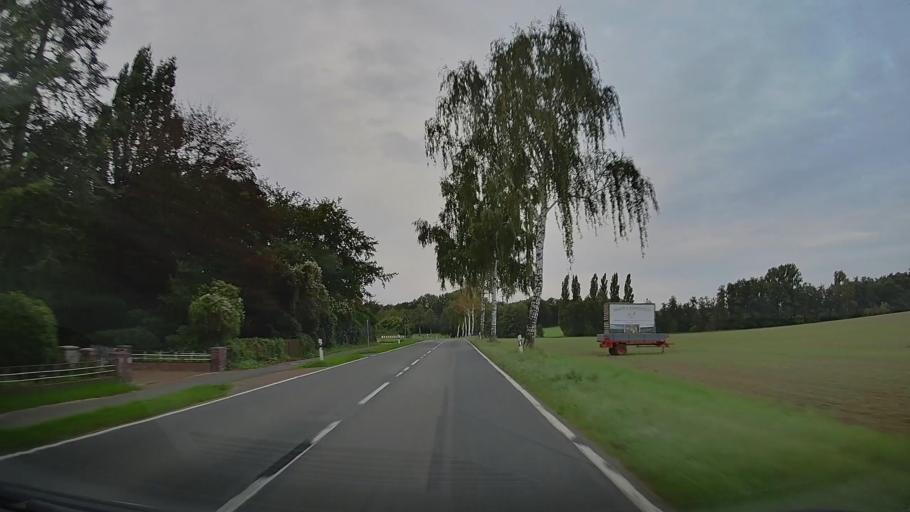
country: DE
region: Lower Saxony
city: Sustedt
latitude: 52.9012
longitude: 8.8948
